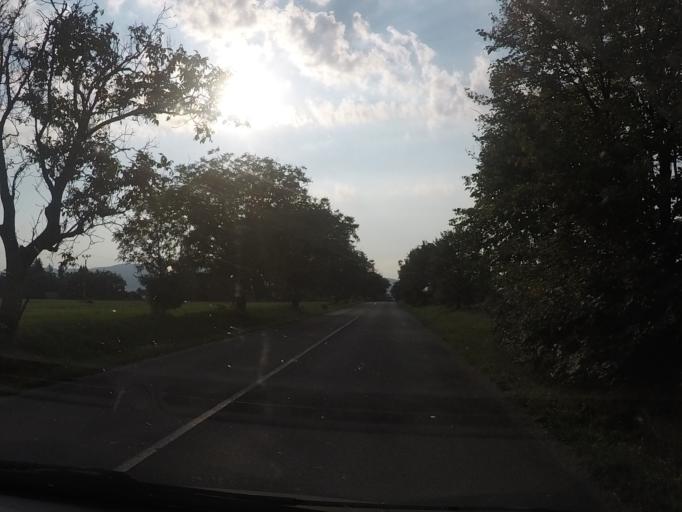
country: SK
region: Nitriansky
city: Zlate Moravce
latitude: 48.3881
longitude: 18.3670
